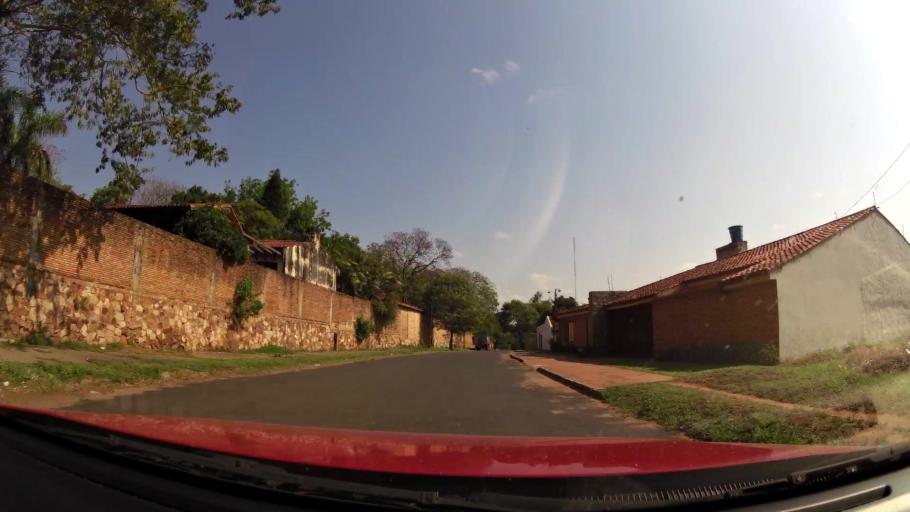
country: PY
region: Asuncion
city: Asuncion
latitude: -25.3224
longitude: -57.6313
